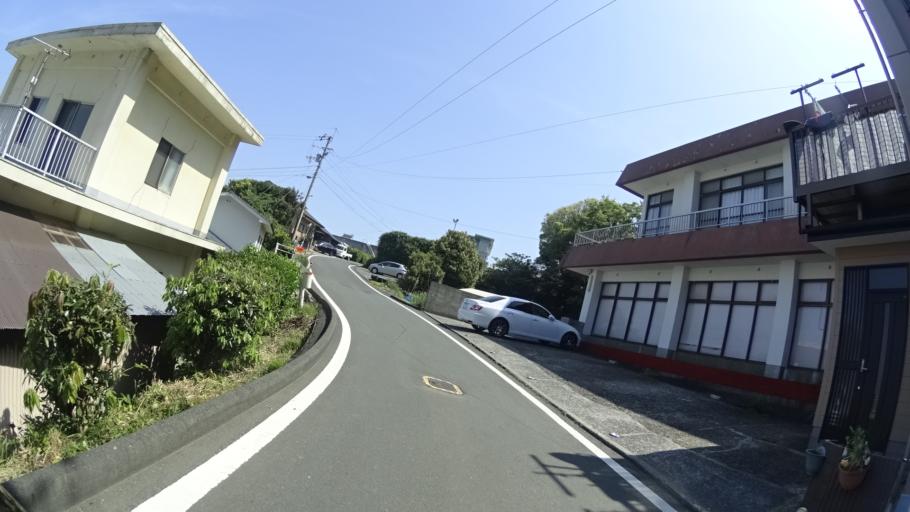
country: JP
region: Ehime
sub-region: Nishiuwa-gun
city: Ikata-cho
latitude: 33.3695
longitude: 132.0503
